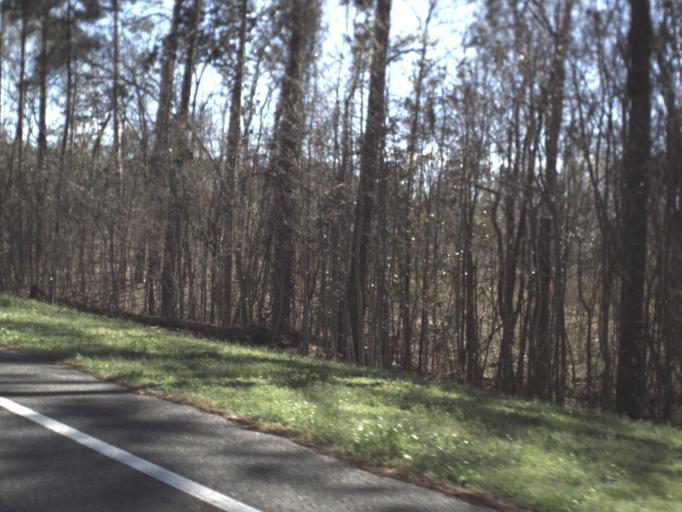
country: US
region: Florida
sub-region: Gadsden County
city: Midway
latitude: 30.5199
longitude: -84.4675
